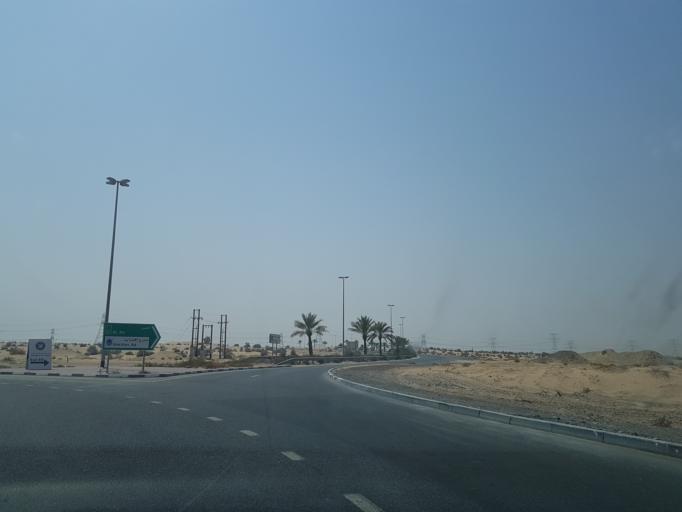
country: AE
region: Ash Shariqah
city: Sharjah
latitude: 25.1225
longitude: 55.4266
